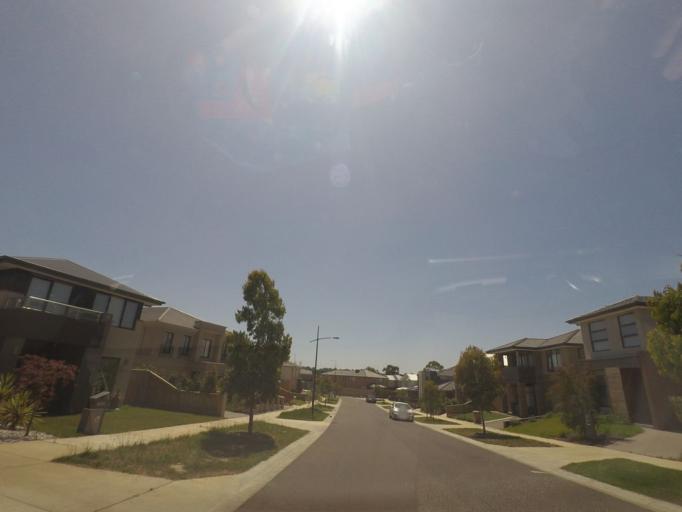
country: AU
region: Victoria
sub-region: Knox
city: Wantirna
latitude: -37.8595
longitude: 145.2149
